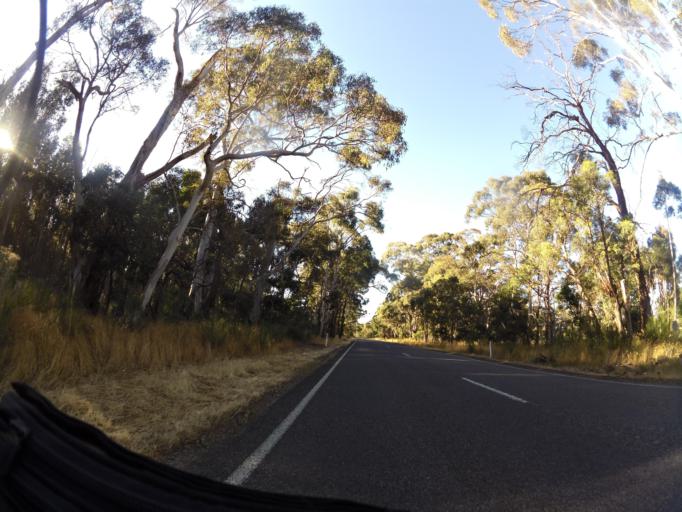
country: AU
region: Victoria
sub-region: Ballarat North
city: Delacombe
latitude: -37.4540
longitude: 143.3806
